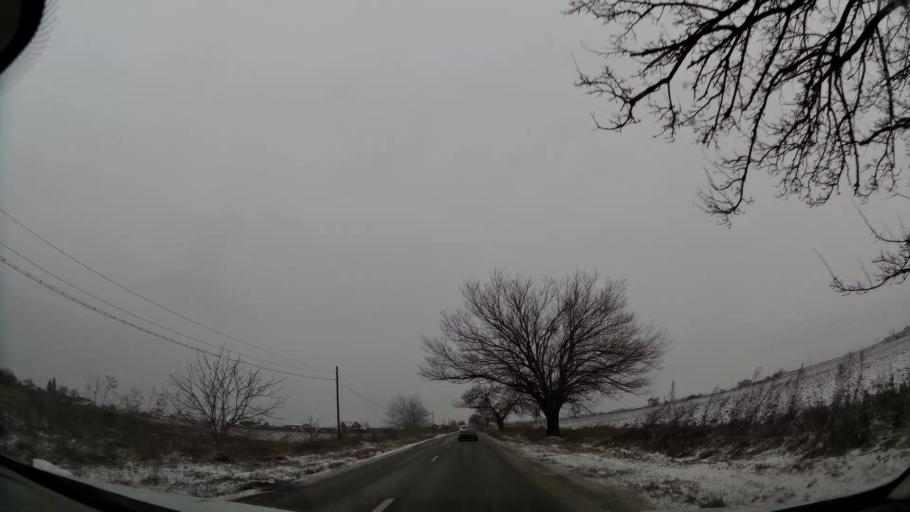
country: RO
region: Dambovita
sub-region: Comuna Ulmi
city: Ulmi
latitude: 44.8908
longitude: 25.5183
